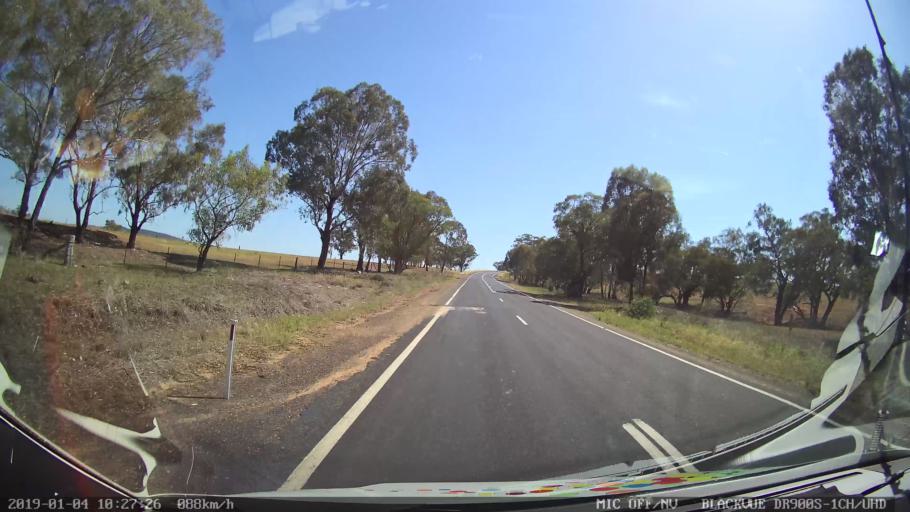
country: AU
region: New South Wales
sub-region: Cabonne
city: Canowindra
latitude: -33.3703
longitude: 148.5986
